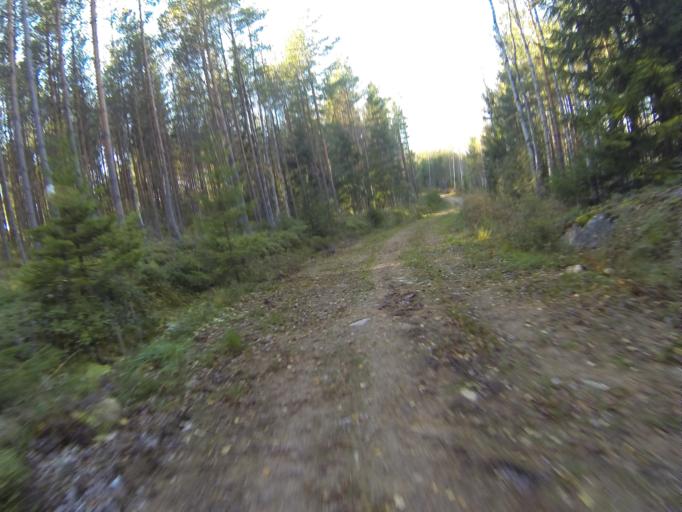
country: FI
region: Varsinais-Suomi
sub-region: Salo
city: Saerkisalo
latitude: 60.2242
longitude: 22.9545
